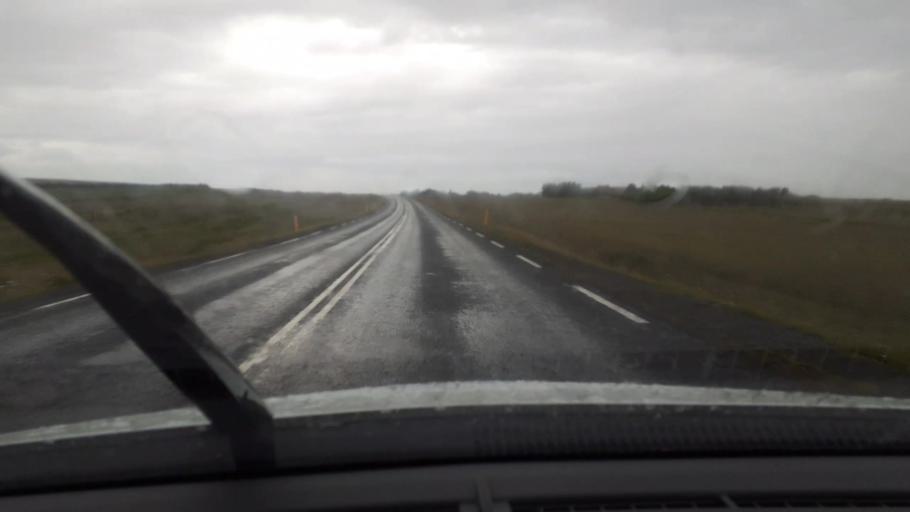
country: IS
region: West
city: Akranes
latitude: 64.3656
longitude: -21.9320
